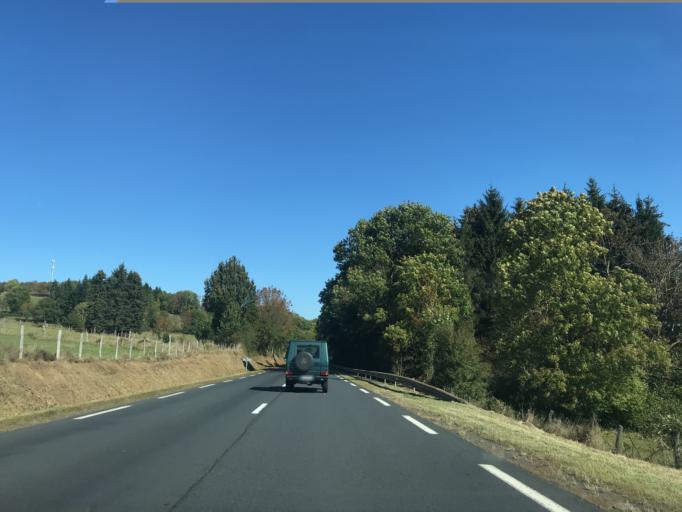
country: FR
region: Auvergne
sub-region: Departement du Puy-de-Dome
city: Gelles
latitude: 45.7300
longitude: 2.8048
